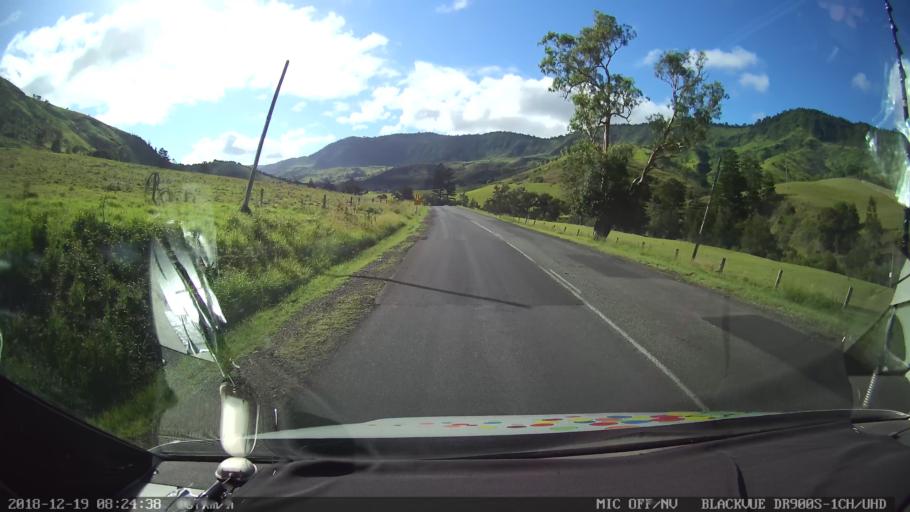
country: AU
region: New South Wales
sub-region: Kyogle
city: Kyogle
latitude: -28.3119
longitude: 152.9136
